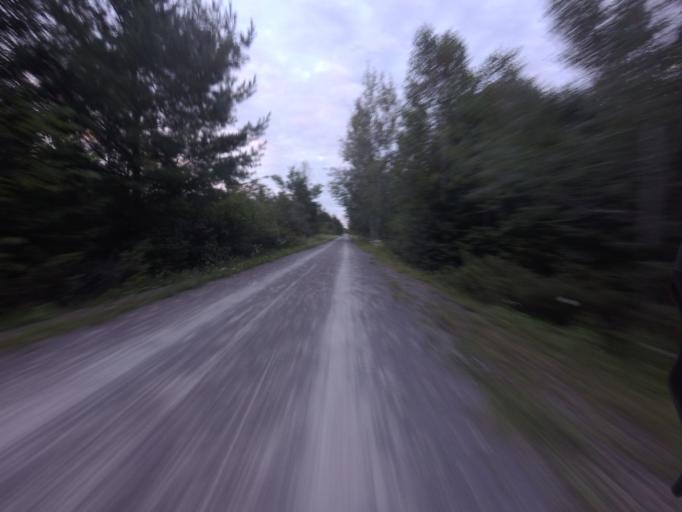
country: CA
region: Ontario
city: Bells Corners
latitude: 45.2442
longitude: -75.9430
